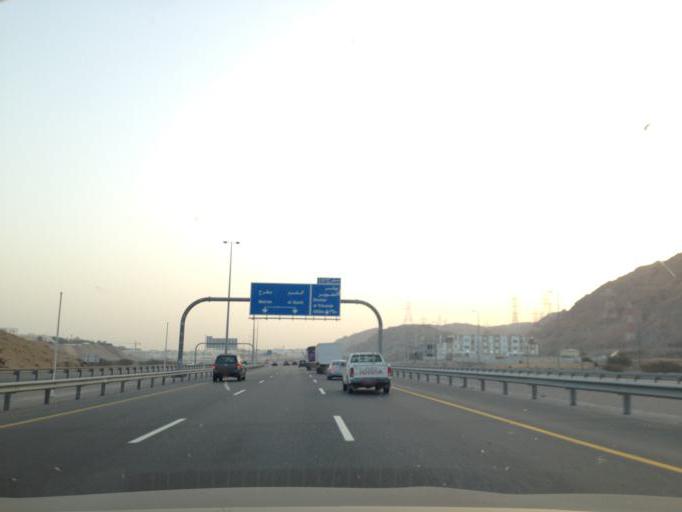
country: OM
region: Muhafazat Masqat
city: Bawshar
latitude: 23.5755
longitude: 58.4348
